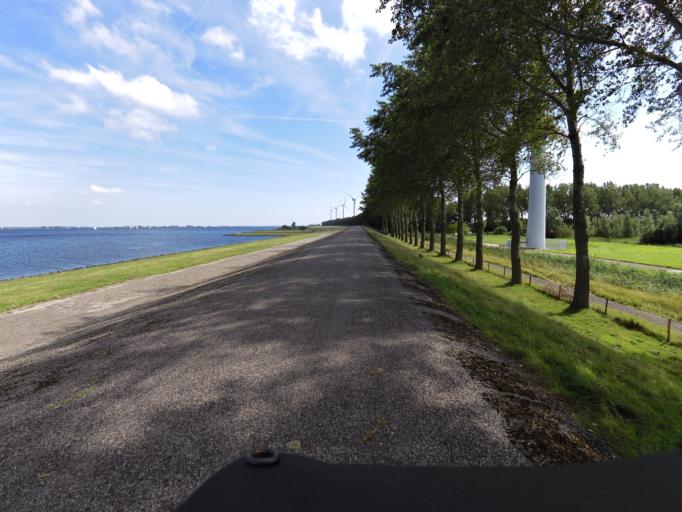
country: NL
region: South Holland
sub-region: Gemeente Goeree-Overflakkee
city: Middelharnis
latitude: 51.7584
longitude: 4.2140
